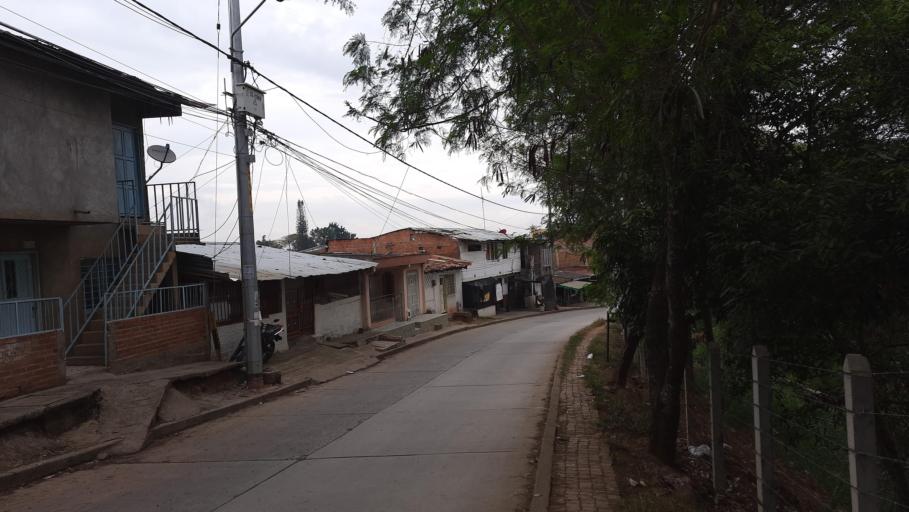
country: CO
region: Valle del Cauca
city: Cali
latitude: 3.3774
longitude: -76.5602
